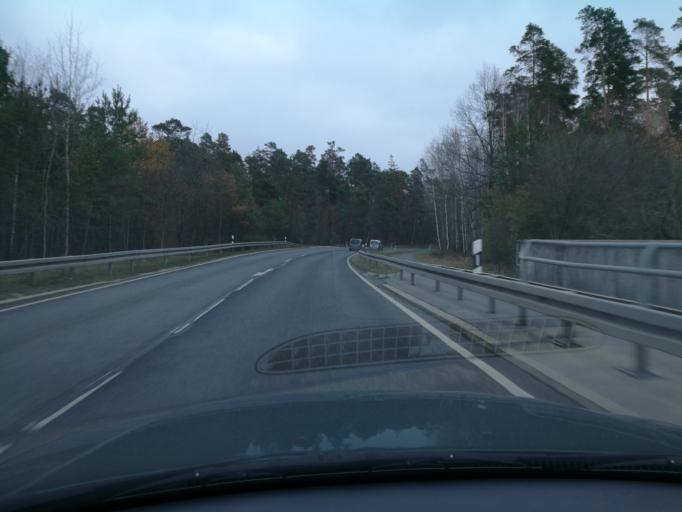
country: DE
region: Bavaria
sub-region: Regierungsbezirk Mittelfranken
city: Feucht
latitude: 49.3911
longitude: 11.1888
